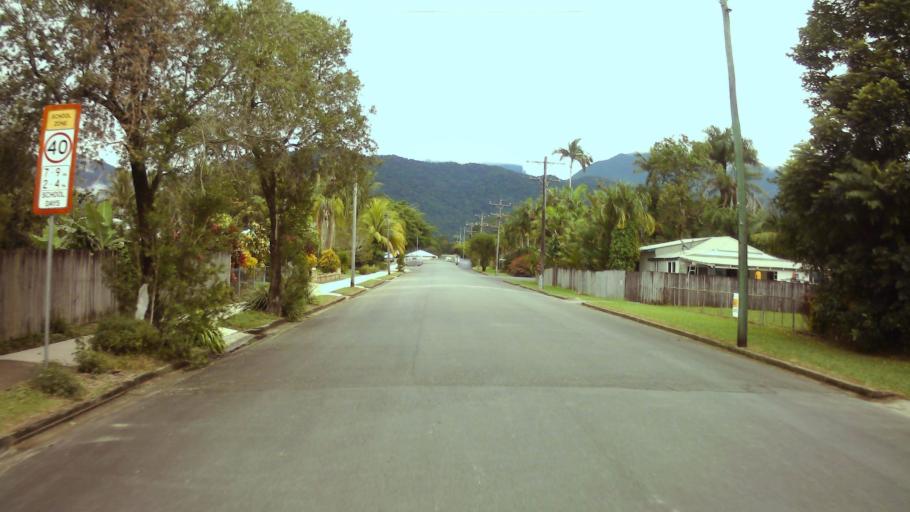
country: AU
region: Queensland
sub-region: Cairns
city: Port Douglas
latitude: -16.4619
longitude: 145.3712
